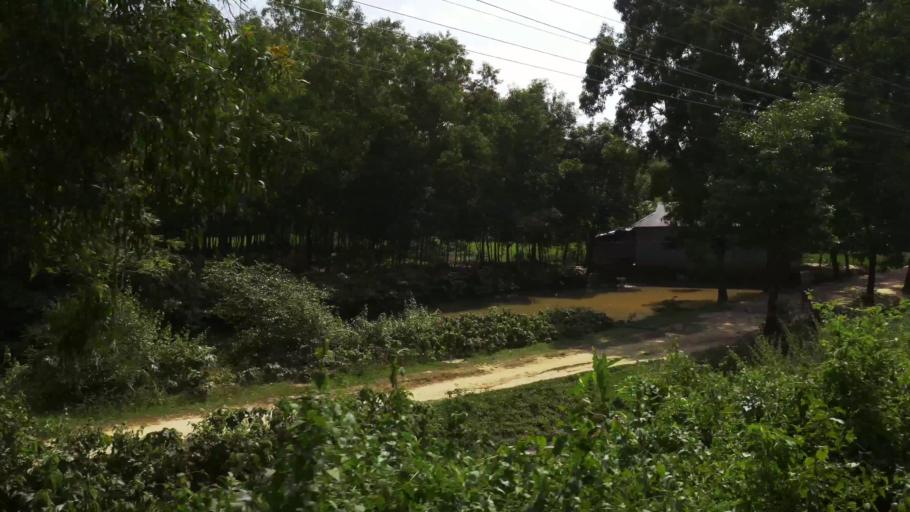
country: BD
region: Dhaka
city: Gafargaon
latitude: 24.2082
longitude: 90.4824
